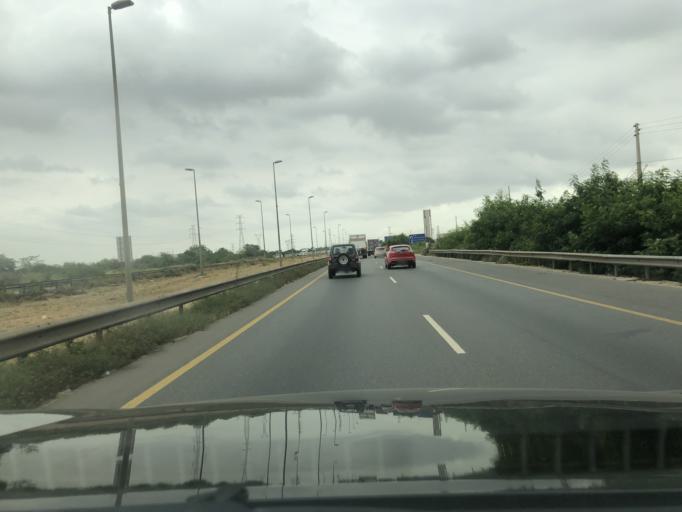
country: AO
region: Luanda
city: Luanda
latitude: -8.9729
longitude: 13.2682
